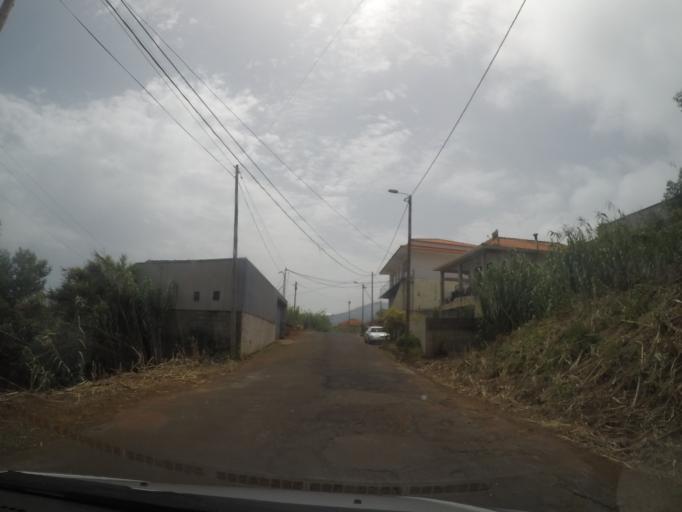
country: PT
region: Madeira
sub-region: Santa Cruz
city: Santa Cruz
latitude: 32.7023
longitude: -16.7905
